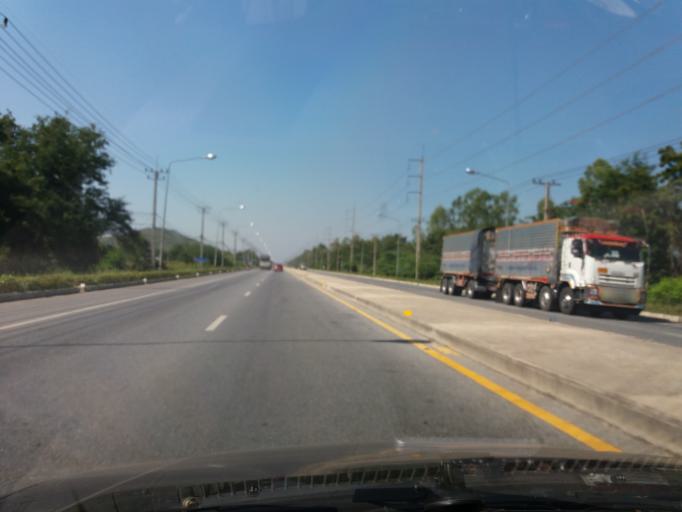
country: TH
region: Chai Nat
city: Chai Nat
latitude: 15.2382
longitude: 100.1044
